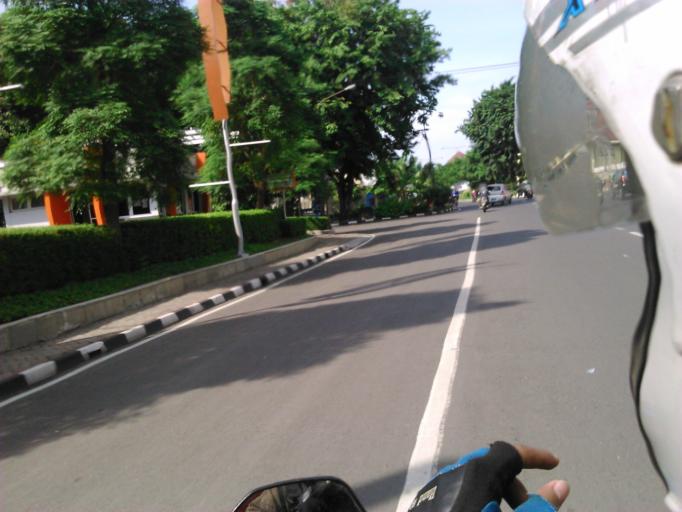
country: ID
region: East Java
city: Mulyorejo
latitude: -7.2768
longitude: 112.7813
